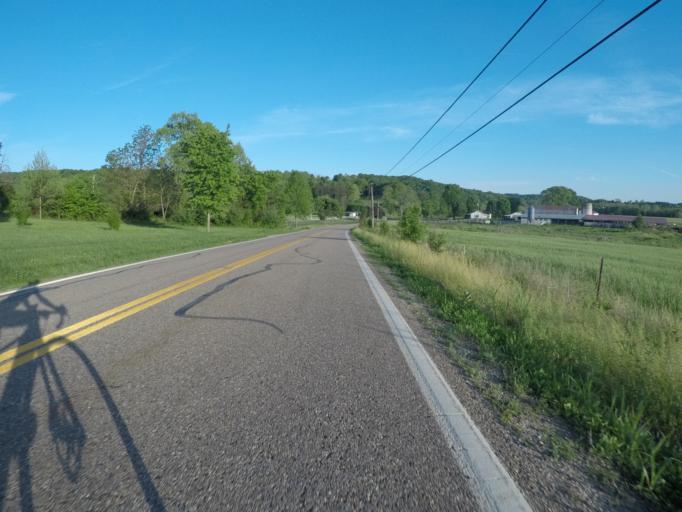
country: US
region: West Virginia
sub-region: Cabell County
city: Huntington
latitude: 38.5433
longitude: -82.4621
